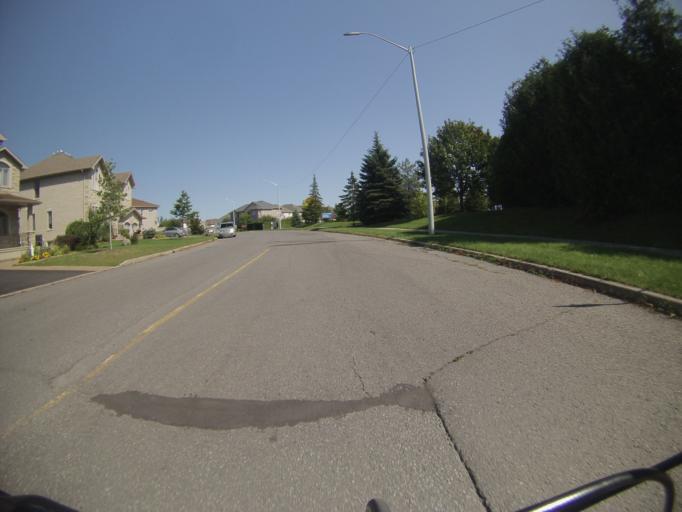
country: CA
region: Ontario
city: Ottawa
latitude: 45.3556
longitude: -75.6364
